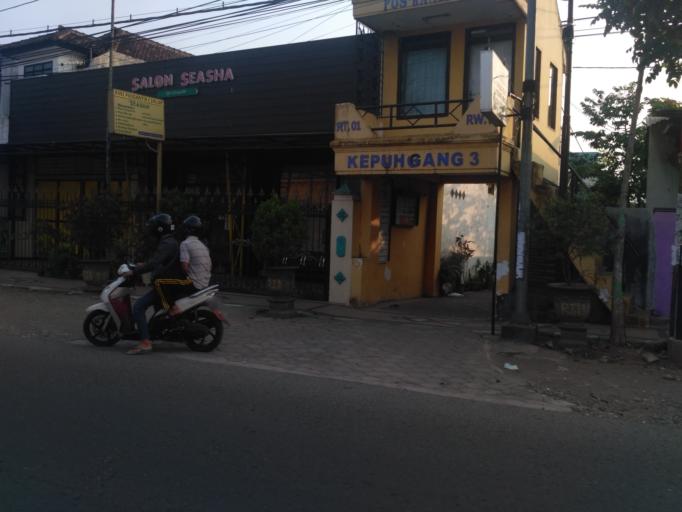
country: ID
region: East Java
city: Kepuh
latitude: -8.0108
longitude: 112.6201
